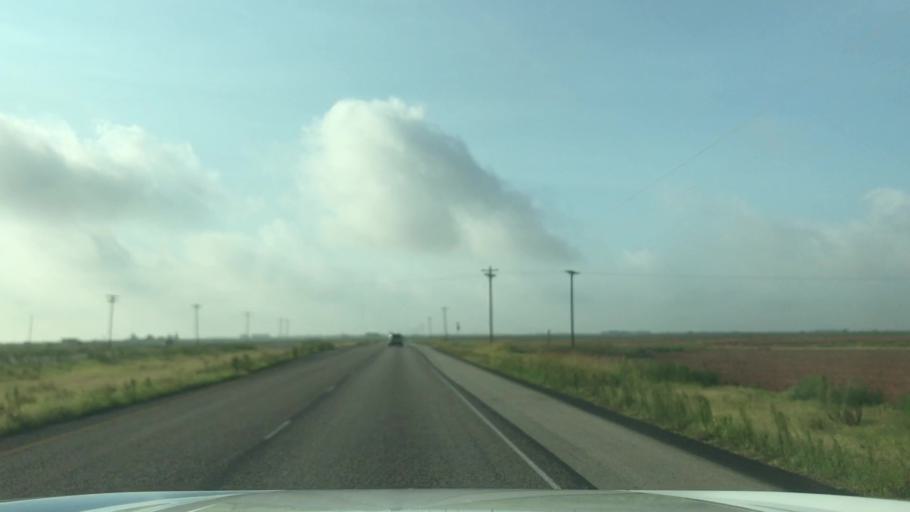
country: US
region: Texas
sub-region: Garza County
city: Post
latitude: 33.2270
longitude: -101.4431
